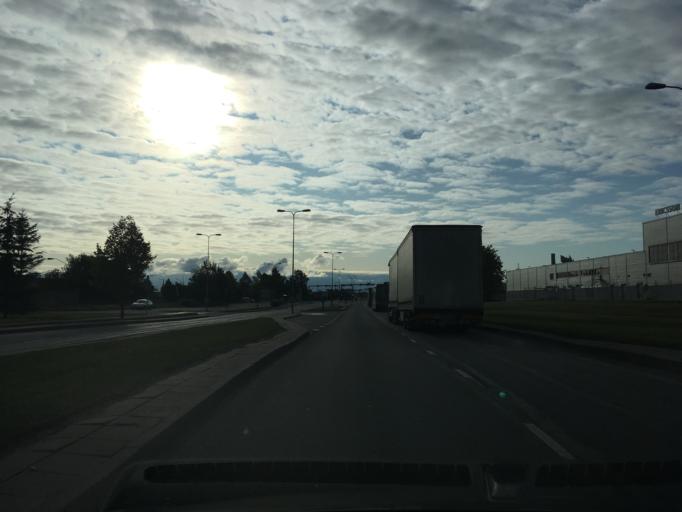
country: EE
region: Harju
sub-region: Tallinna linn
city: Kose
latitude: 59.4319
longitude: 24.8329
